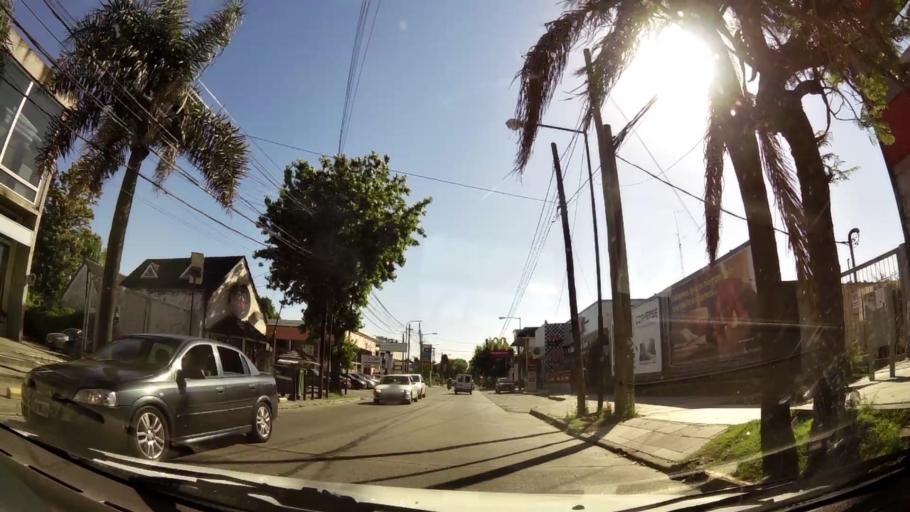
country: AR
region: Buenos Aires
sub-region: Partido de San Isidro
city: San Isidro
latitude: -34.4805
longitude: -58.5540
